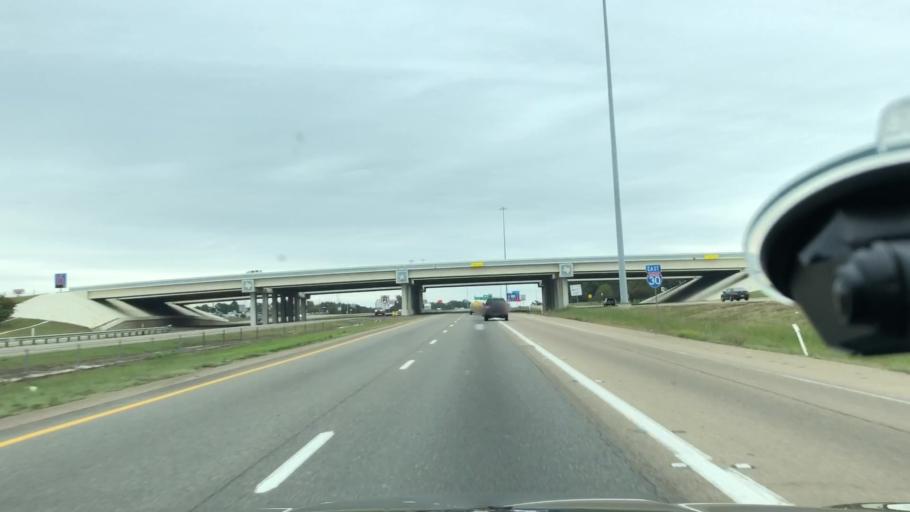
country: US
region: Arkansas
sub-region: Miller County
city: Texarkana
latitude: 33.4646
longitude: -94.0680
